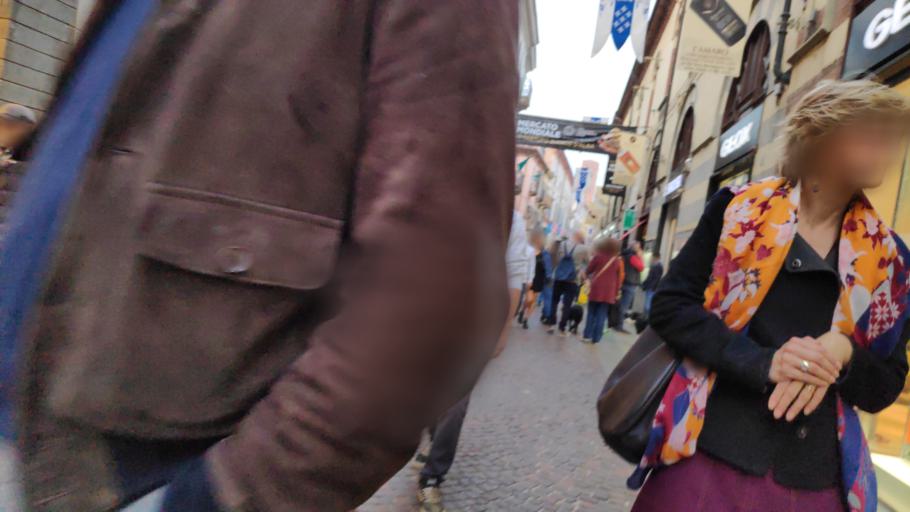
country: IT
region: Piedmont
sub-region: Provincia di Cuneo
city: Alba
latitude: 44.6987
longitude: 8.0346
